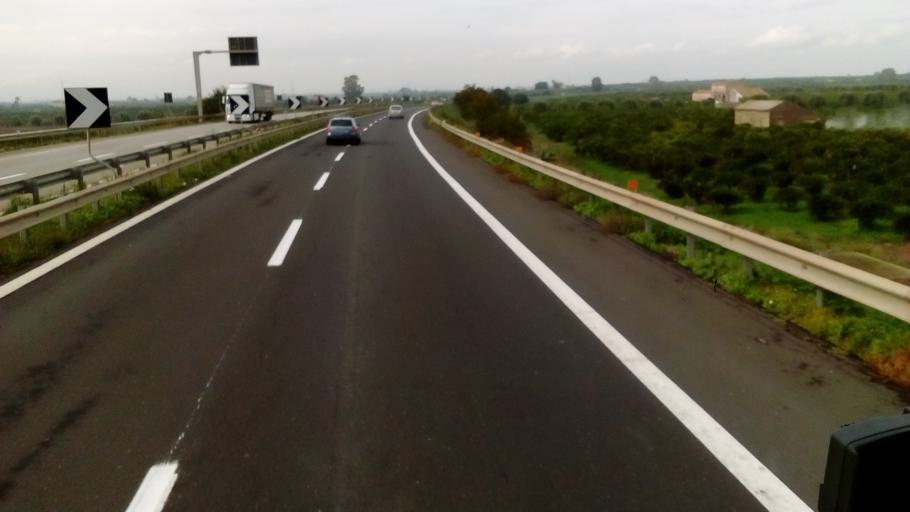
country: IT
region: Sicily
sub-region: Catania
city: Motta Sant'Anastasia
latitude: 37.4636
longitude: 14.9264
